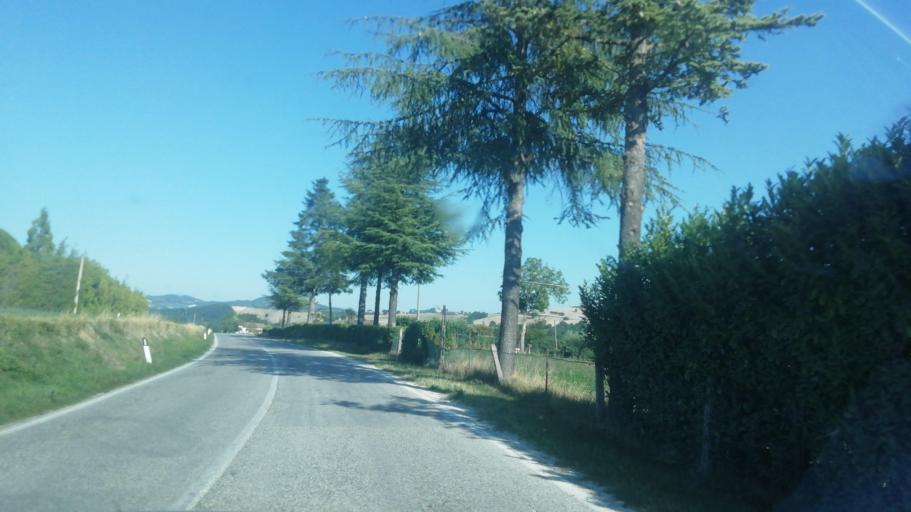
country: IT
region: The Marches
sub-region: Provincia di Pesaro e Urbino
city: Pergola
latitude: 43.5471
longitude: 12.7882
